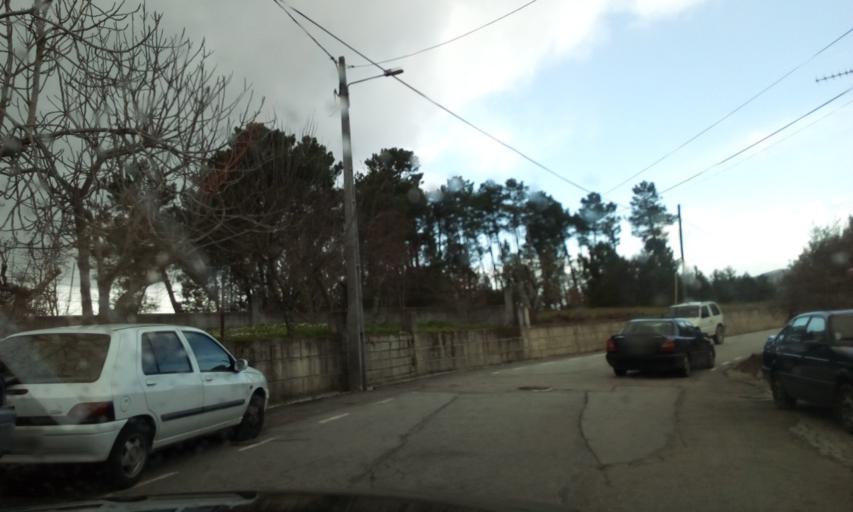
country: PT
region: Guarda
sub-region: Fornos de Algodres
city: Fornos de Algodres
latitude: 40.6381
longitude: -7.5844
